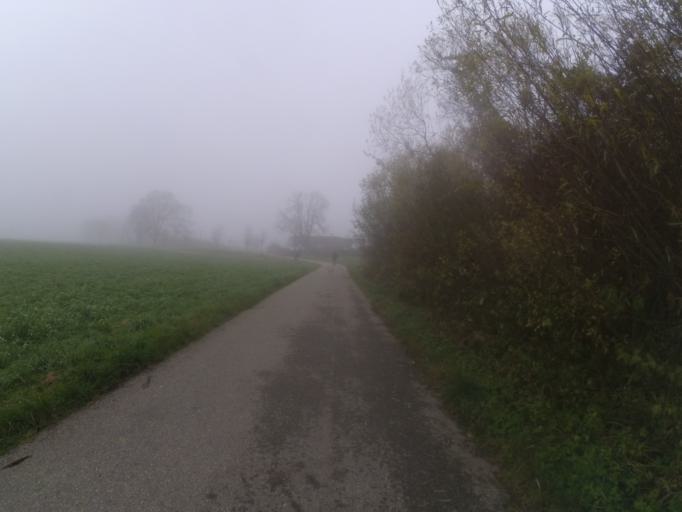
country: DE
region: Bavaria
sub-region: Swabia
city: Neu-Ulm
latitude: 48.3731
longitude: 10.0135
